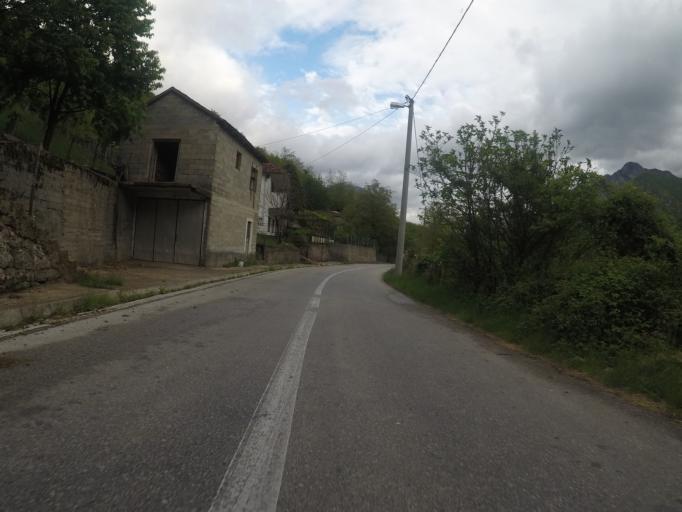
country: BA
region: Federation of Bosnia and Herzegovina
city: Siroki Brijeg
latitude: 43.5388
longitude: 17.6014
